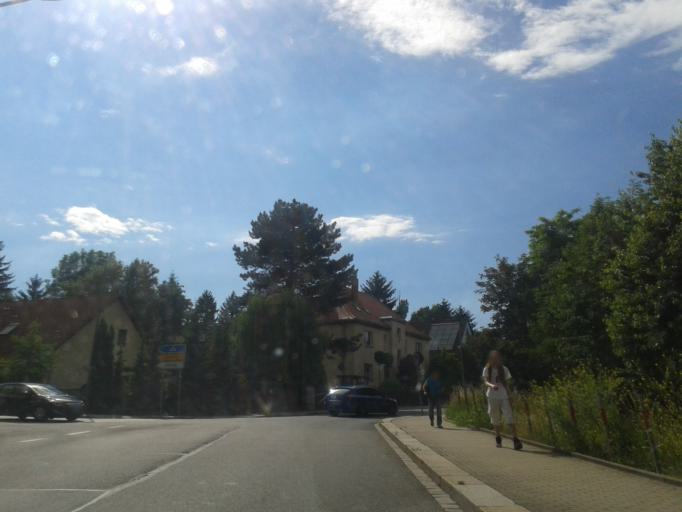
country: DE
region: Saxony
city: Radebeul
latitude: 51.0529
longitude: 13.6732
